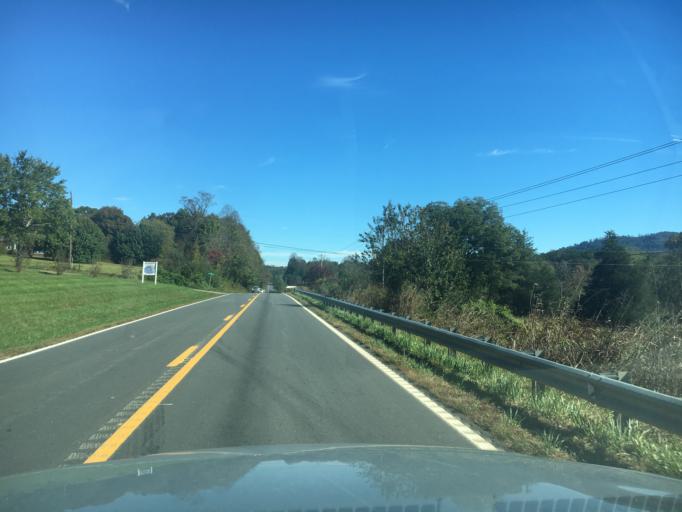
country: US
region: North Carolina
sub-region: Burke County
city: Glen Alpine
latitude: 35.6454
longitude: -81.7699
